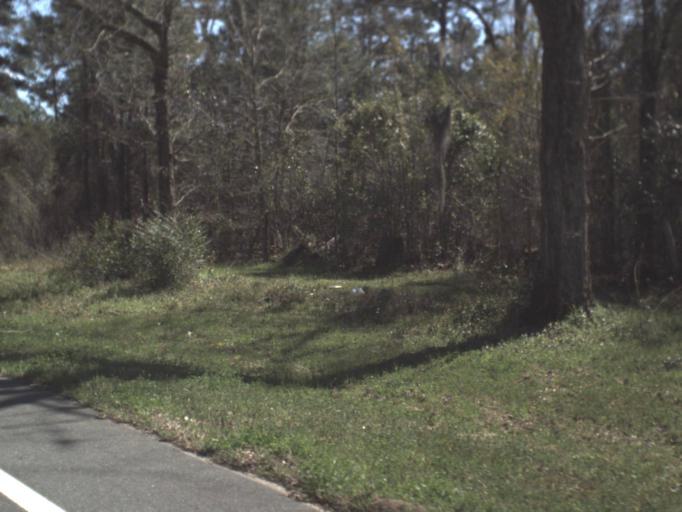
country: US
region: Florida
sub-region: Gadsden County
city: Gretna
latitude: 30.6829
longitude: -84.7140
